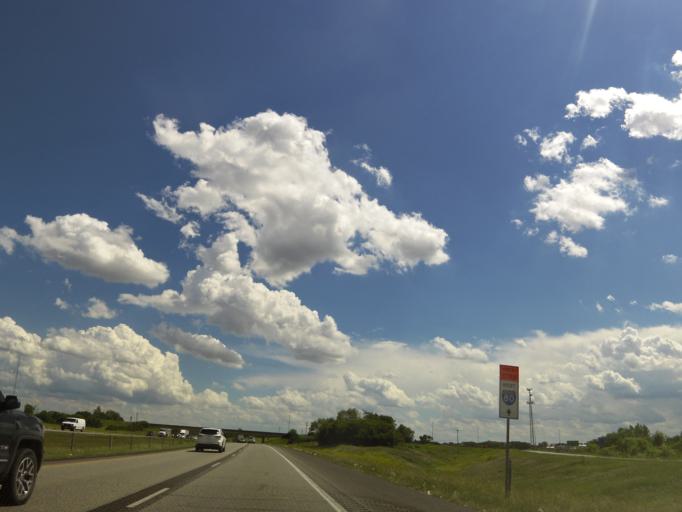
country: US
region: Iowa
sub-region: Linn County
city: Ely
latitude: 41.8508
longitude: -91.6681
